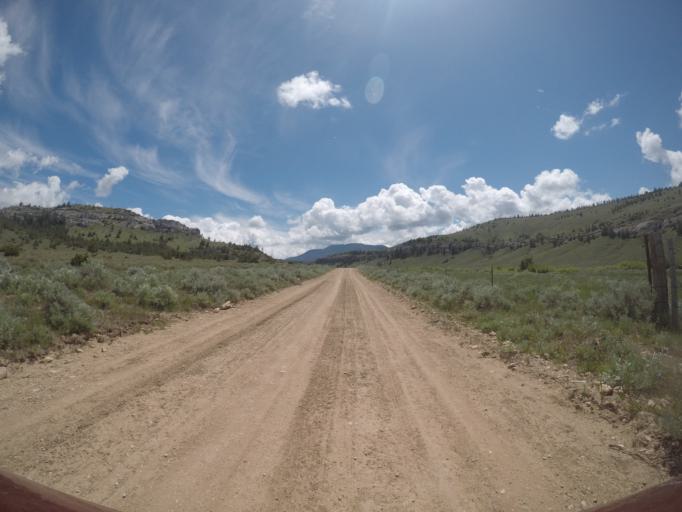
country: US
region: Montana
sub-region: Yellowstone County
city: Laurel
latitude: 45.2365
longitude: -108.6230
